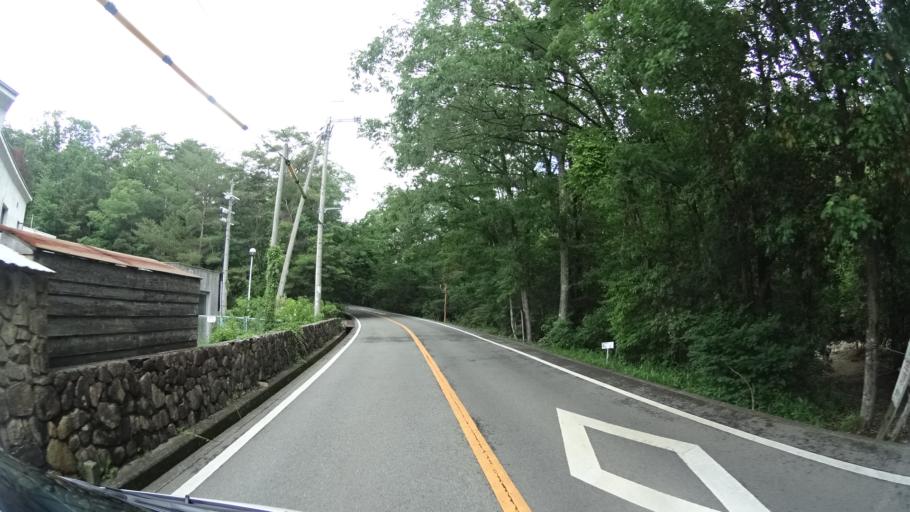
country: JP
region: Kyoto
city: Kameoka
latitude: 35.0054
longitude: 135.4337
